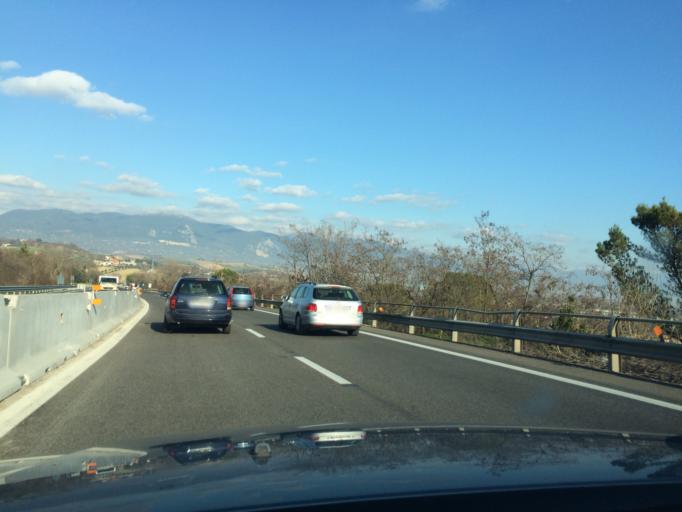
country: IT
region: Umbria
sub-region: Provincia di Terni
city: Narni Scalo
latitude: 42.5420
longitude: 12.5171
